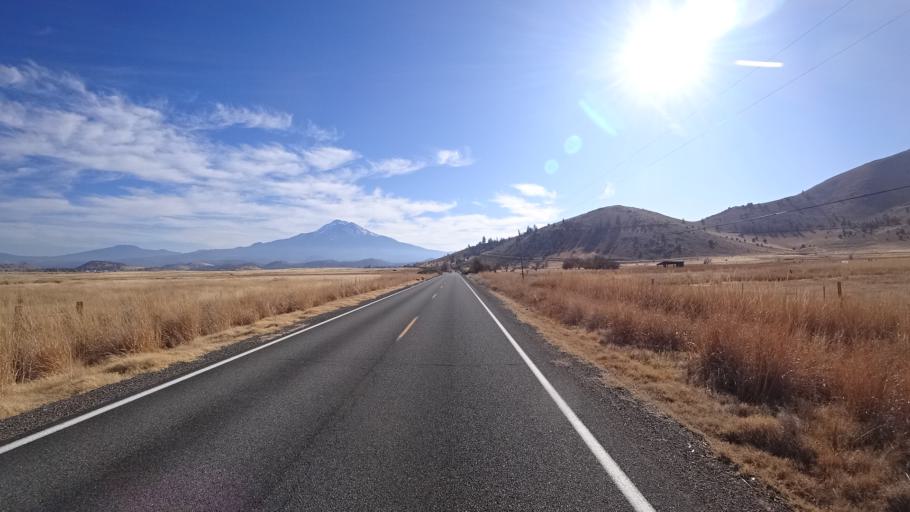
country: US
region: California
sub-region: Siskiyou County
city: Weed
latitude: 41.4716
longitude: -122.4779
